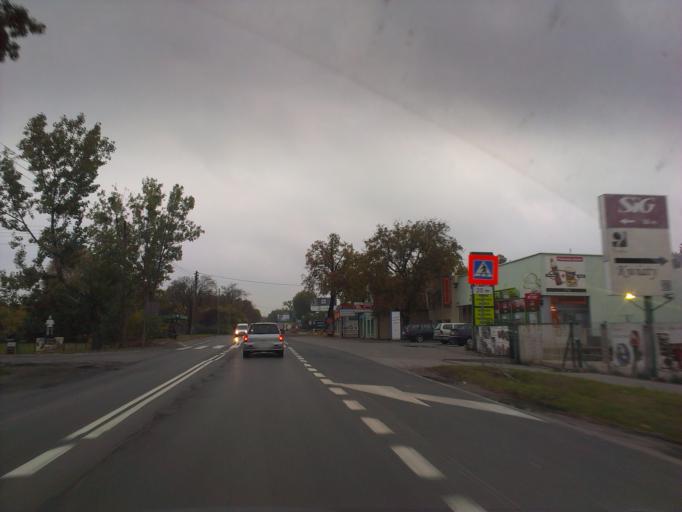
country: PL
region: Greater Poland Voivodeship
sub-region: Powiat poznanski
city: Suchy Las
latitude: 52.4513
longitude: 16.9046
